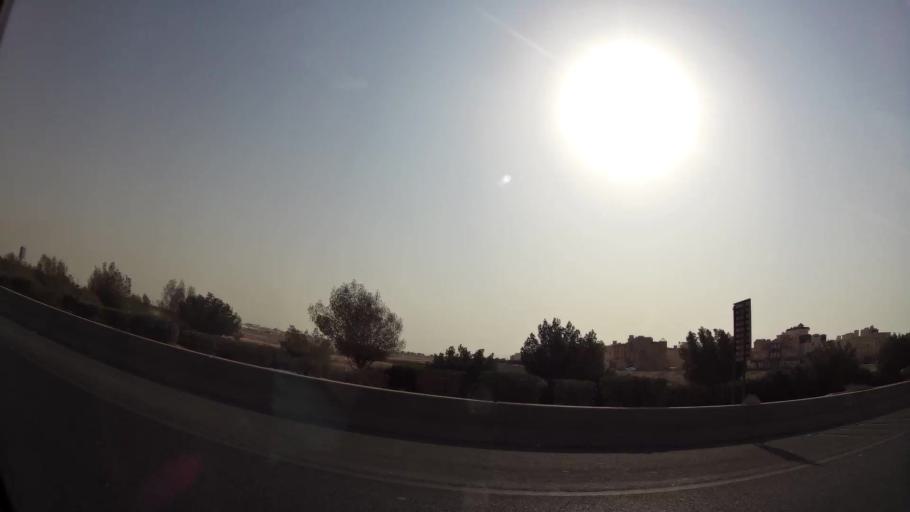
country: KW
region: Muhafazat al Jahra'
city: Al Jahra'
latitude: 29.3256
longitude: 47.7462
